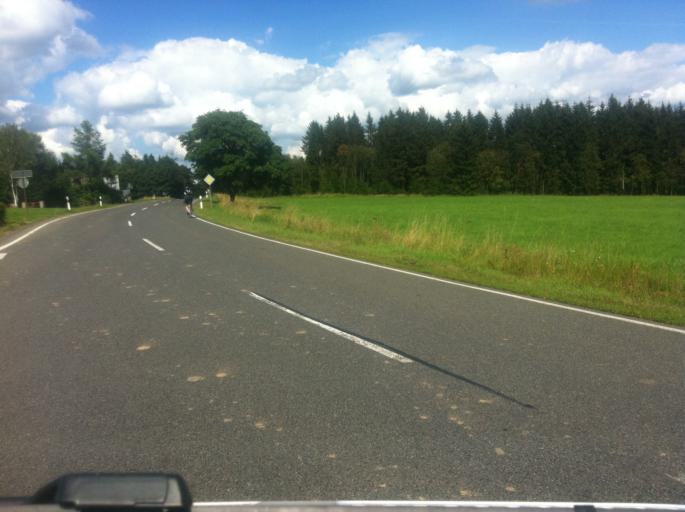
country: DE
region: Rheinland-Pfalz
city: Scheid
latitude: 50.3809
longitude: 6.3435
